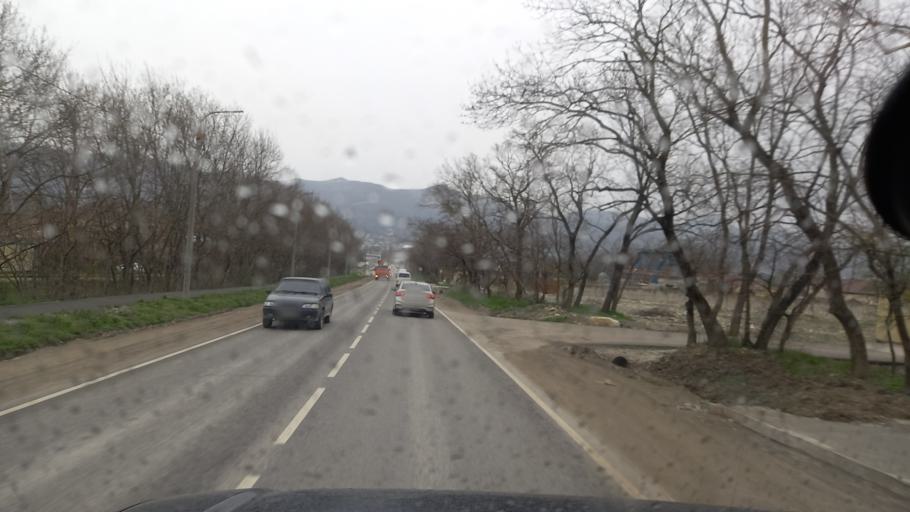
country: RU
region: Krasnodarskiy
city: Gayduk
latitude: 44.7559
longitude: 37.7056
